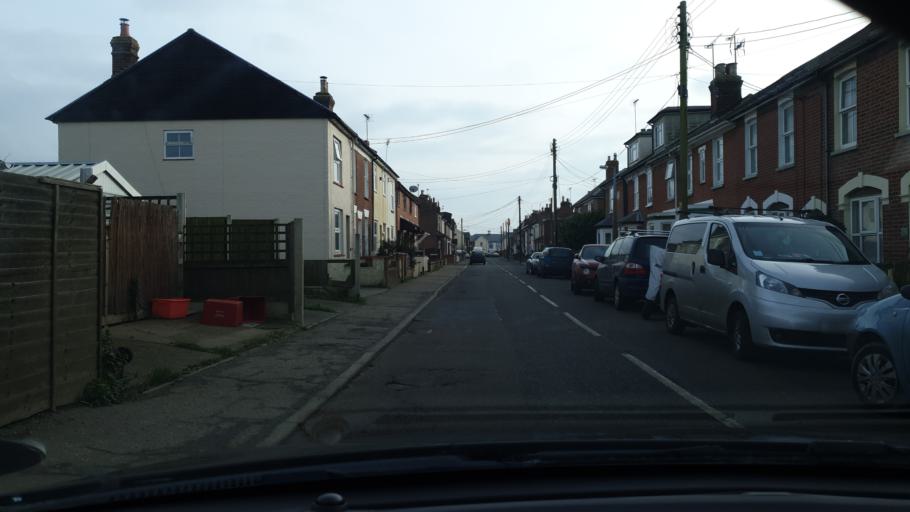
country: GB
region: England
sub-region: Essex
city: Brightlingsea
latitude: 51.8088
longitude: 1.0214
